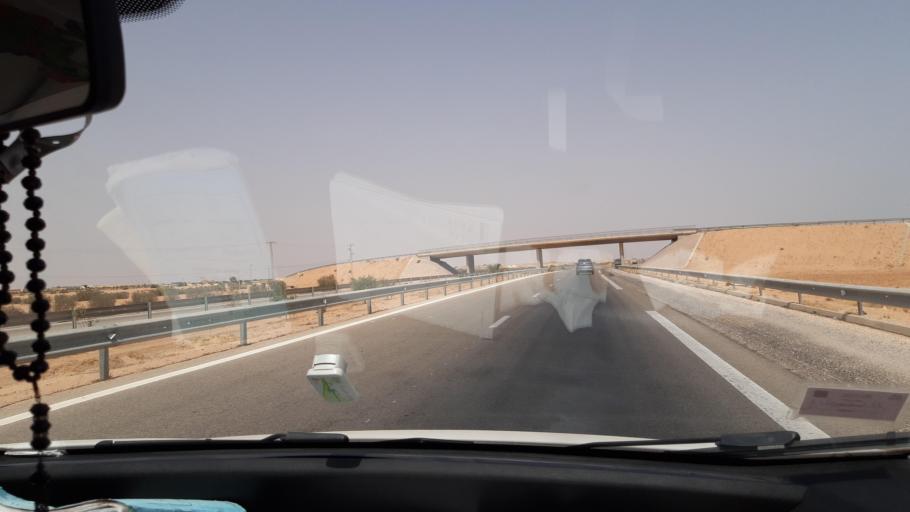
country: TN
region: Safaqis
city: Skhira
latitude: 34.1319
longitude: 9.9571
